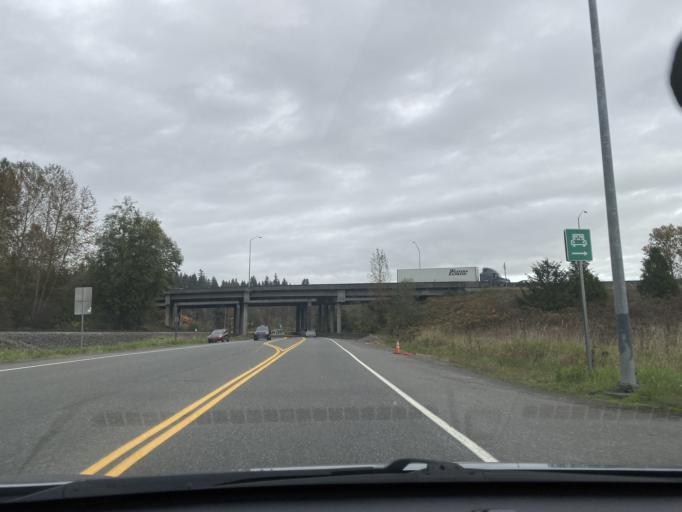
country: US
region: Washington
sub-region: King County
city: Lea Hill
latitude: 47.3005
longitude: -122.1819
